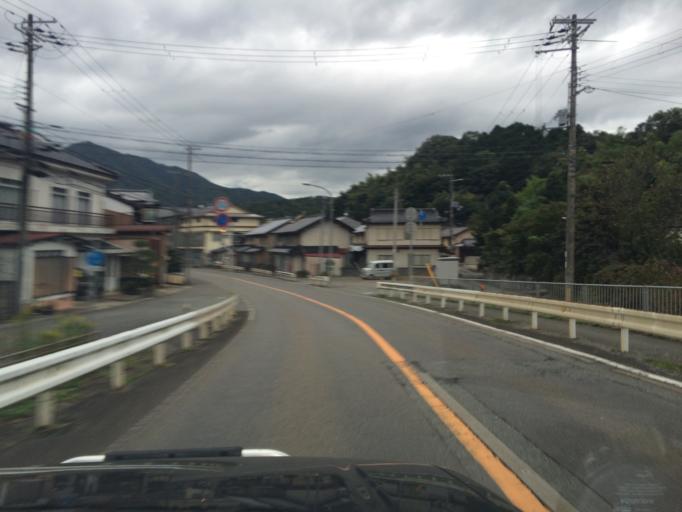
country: JP
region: Hyogo
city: Toyooka
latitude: 35.4282
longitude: 134.7944
